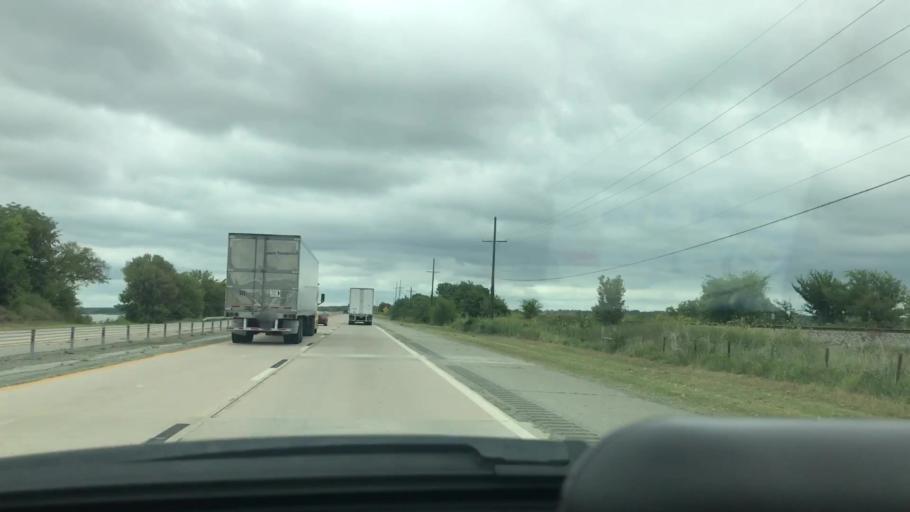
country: US
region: Oklahoma
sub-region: McIntosh County
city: Eufaula
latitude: 35.3272
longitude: -95.5876
